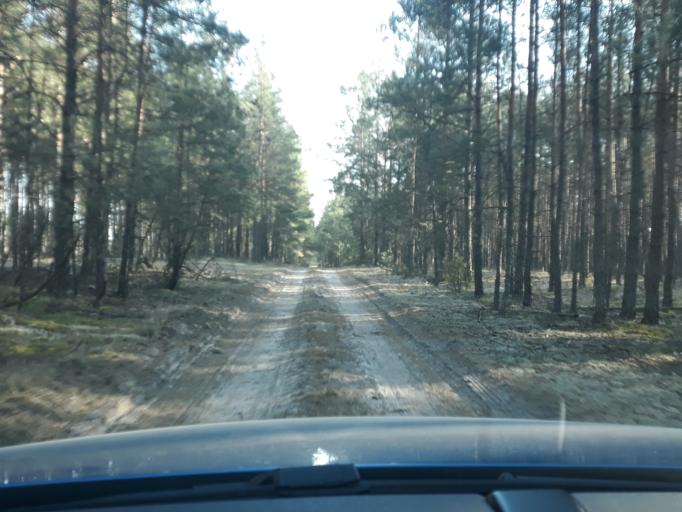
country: PL
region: Pomeranian Voivodeship
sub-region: Powiat bytowski
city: Lipnica
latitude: 53.9103
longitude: 17.4970
